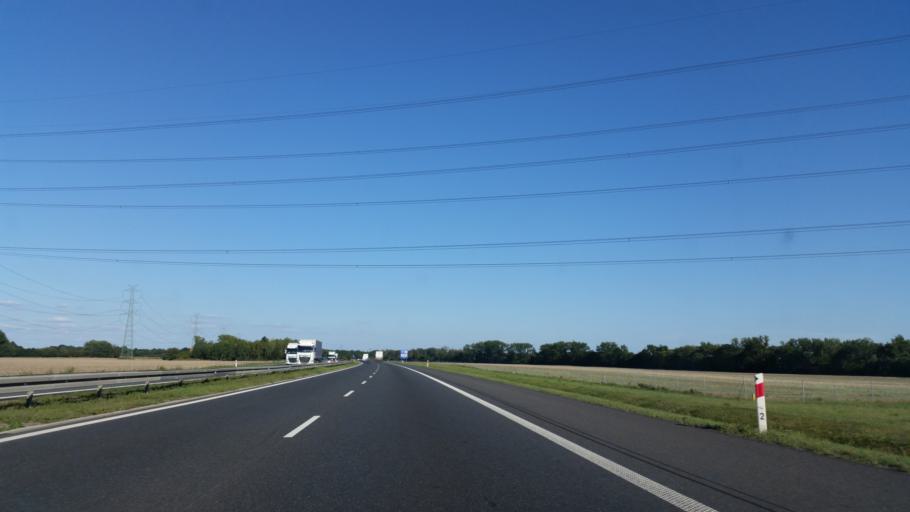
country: PL
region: Opole Voivodeship
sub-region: Powiat brzeski
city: Grodkow
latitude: 50.7718
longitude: 17.3746
